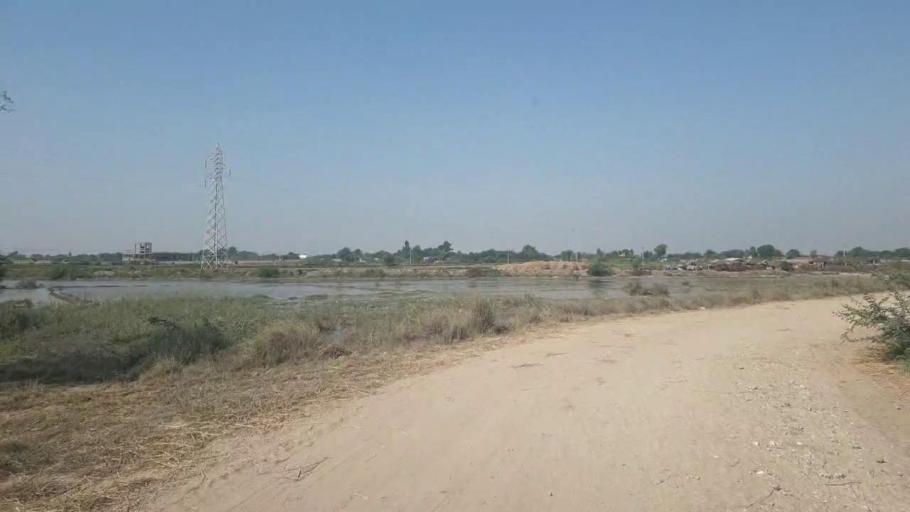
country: PK
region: Sindh
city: Badin
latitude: 24.6749
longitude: 68.8578
